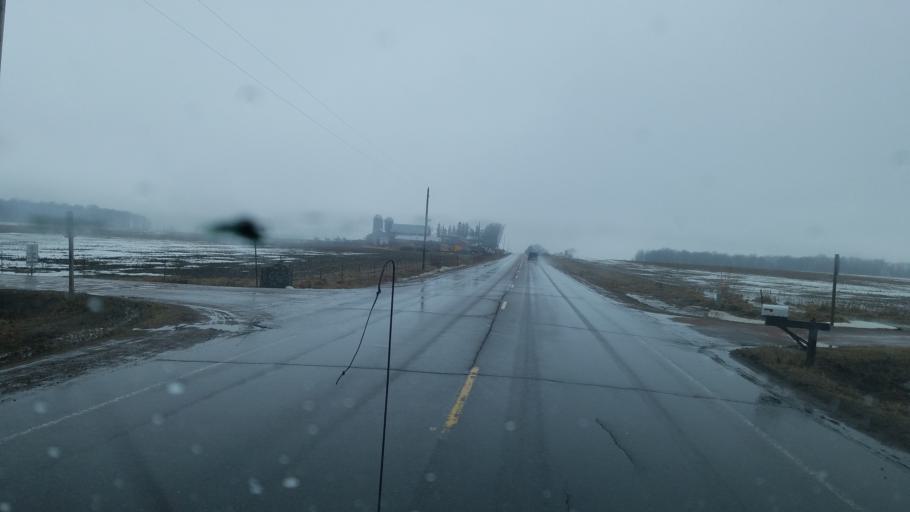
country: US
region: Wisconsin
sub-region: Clark County
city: Loyal
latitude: 44.6548
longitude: -90.3975
